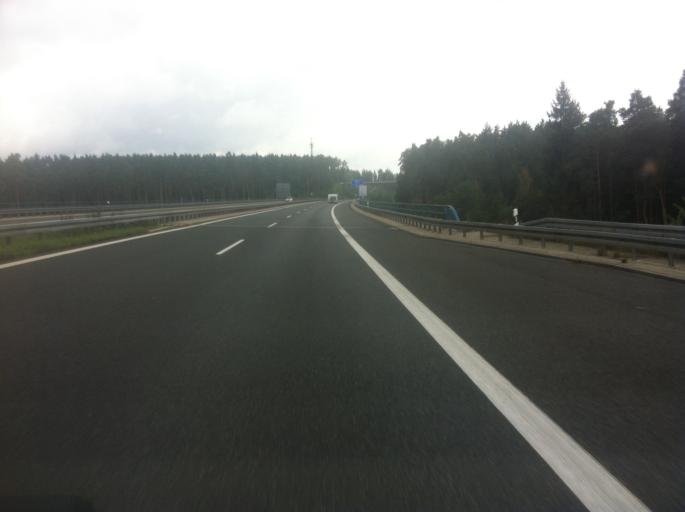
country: DE
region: Bavaria
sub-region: Upper Palatinate
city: Wernberg-Koblitz
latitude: 49.5341
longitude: 12.1905
